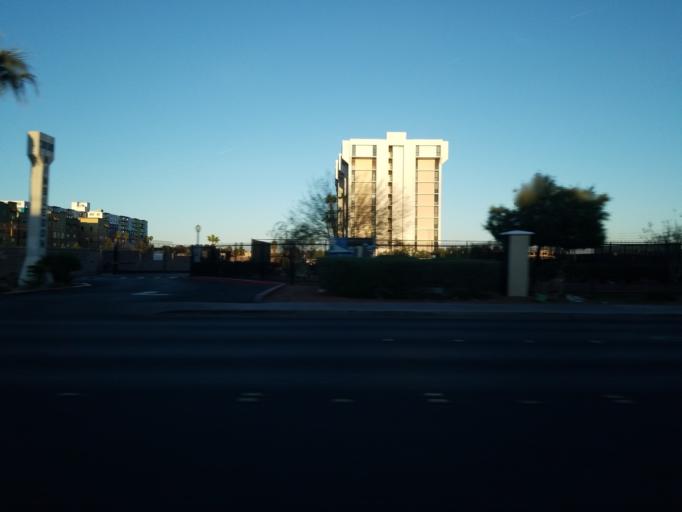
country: US
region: Nevada
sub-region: Clark County
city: Paradise
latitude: 36.1179
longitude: -115.1463
